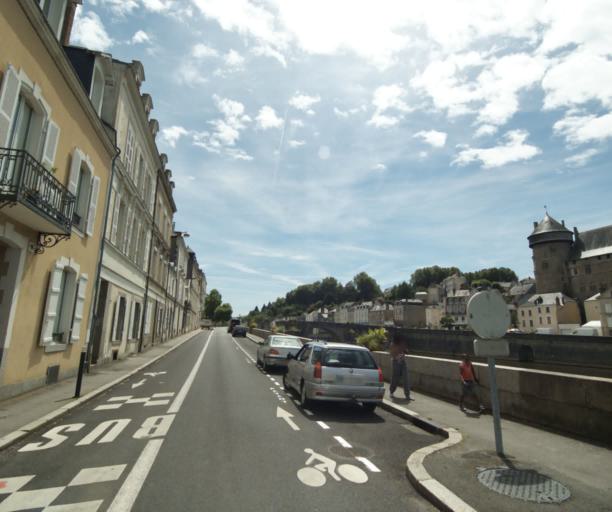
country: FR
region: Pays de la Loire
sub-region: Departement de la Mayenne
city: Laval
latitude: 48.0695
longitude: -0.7695
